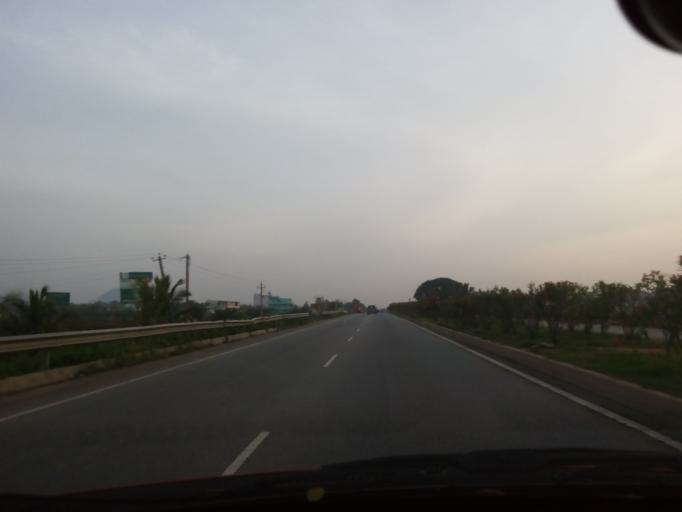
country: IN
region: Karnataka
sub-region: Bangalore Rural
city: Devanhalli
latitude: 13.3246
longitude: 77.7255
